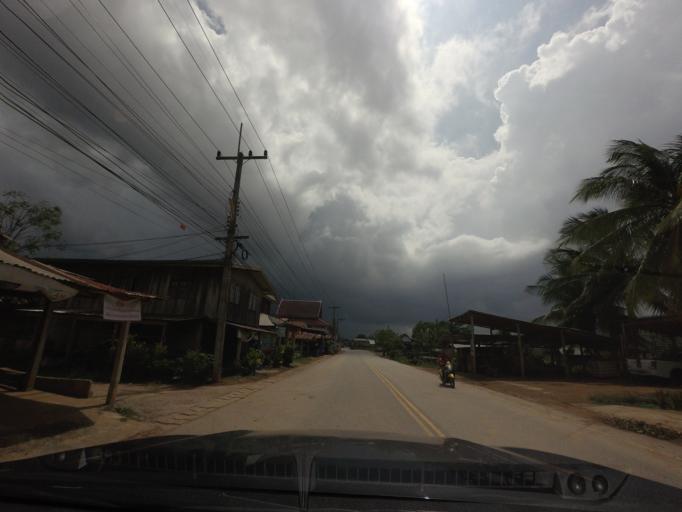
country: LA
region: Vientiane
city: Muang Sanakham
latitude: 17.9914
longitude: 101.7476
